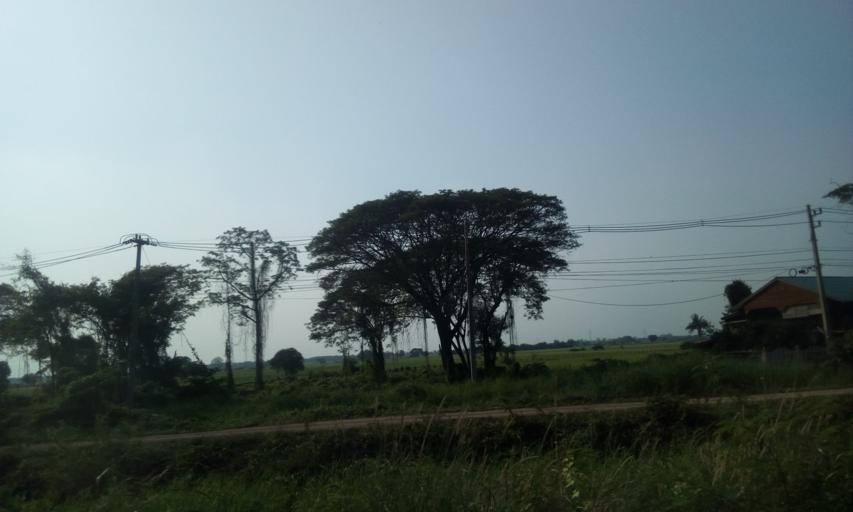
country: TH
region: Sing Buri
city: Phrom Buri
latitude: 14.8107
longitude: 100.4351
